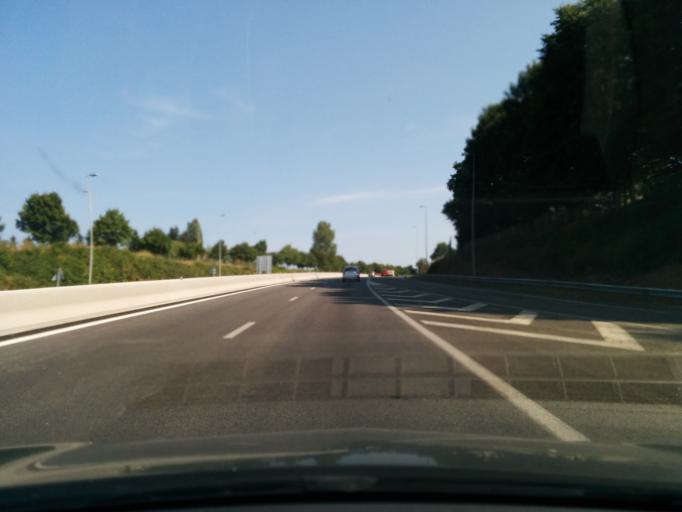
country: FR
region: Limousin
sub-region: Departement de la Haute-Vienne
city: Condat-sur-Vienne
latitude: 45.8172
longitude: 1.2947
